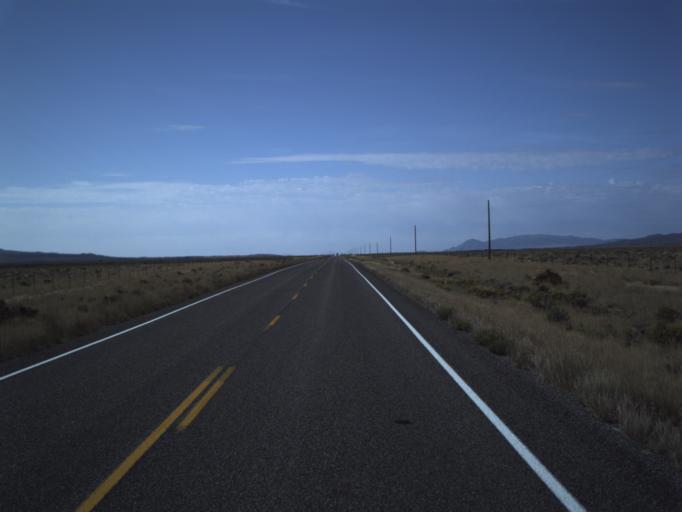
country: US
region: Idaho
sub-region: Cassia County
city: Burley
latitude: 41.7614
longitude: -113.5121
